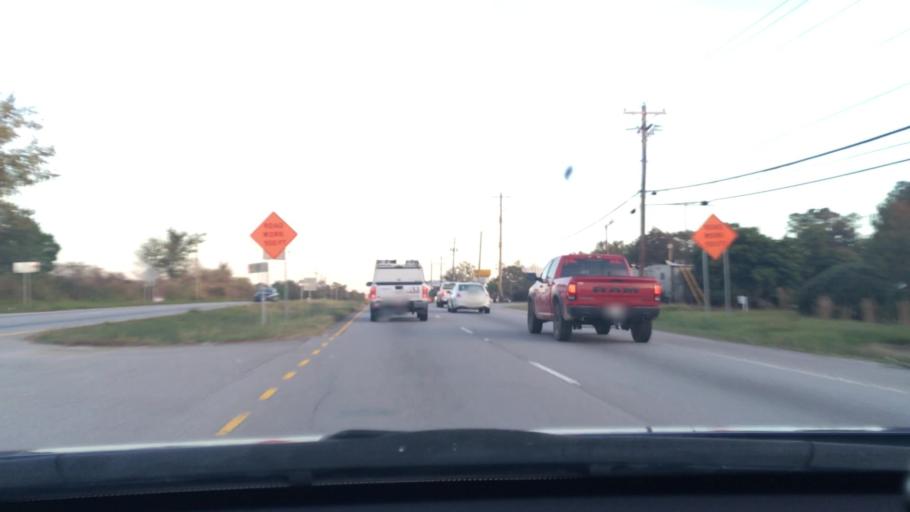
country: US
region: South Carolina
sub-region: Richland County
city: Hopkins
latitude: 33.9523
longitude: -80.9204
